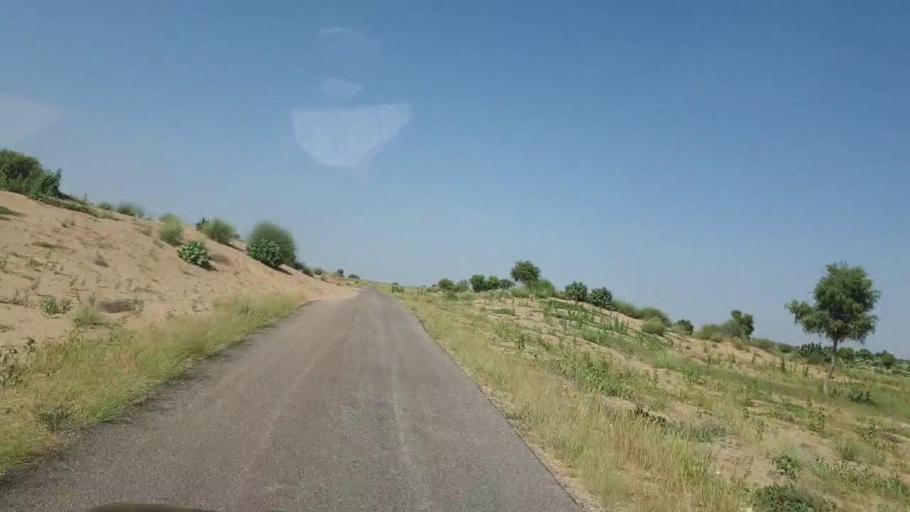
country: PK
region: Sindh
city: Chor
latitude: 25.6315
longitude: 70.3173
